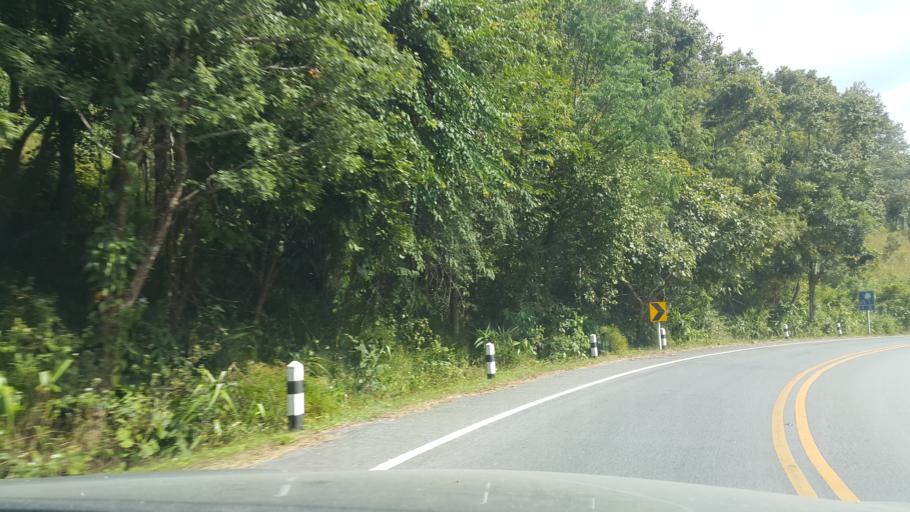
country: TH
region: Phayao
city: Phayao
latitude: 19.0630
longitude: 99.7739
